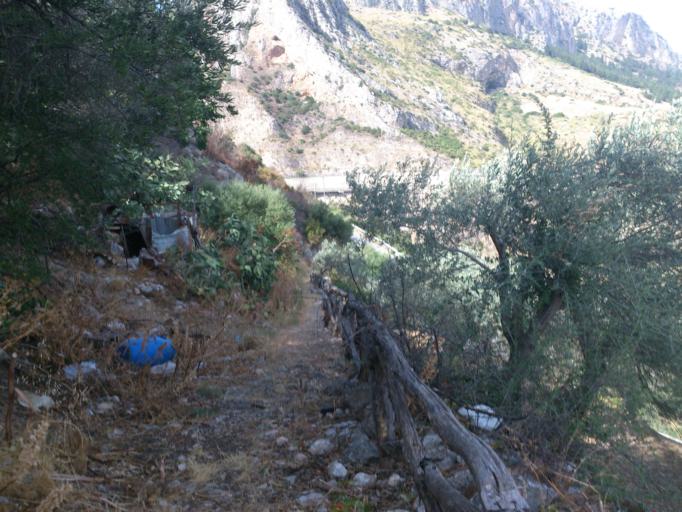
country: IT
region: Calabria
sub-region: Provincia di Reggio Calabria
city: Pazzano
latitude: 38.4694
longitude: 16.4554
